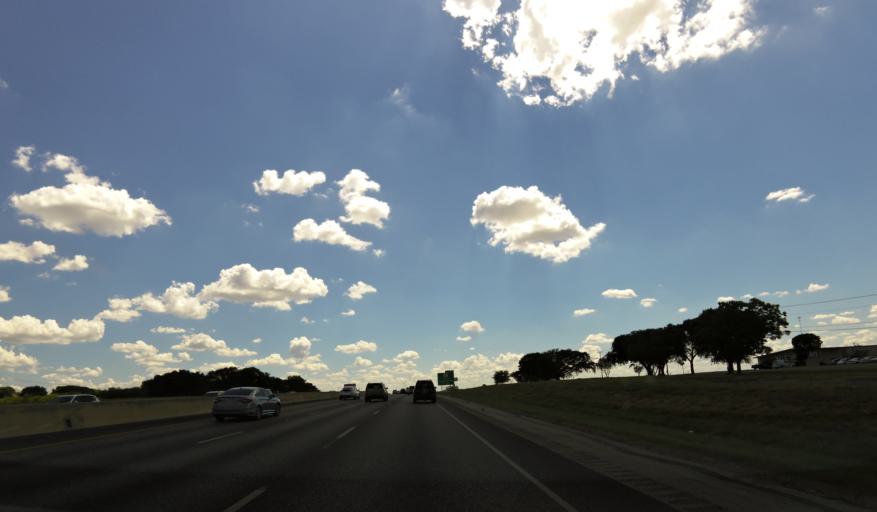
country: US
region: Texas
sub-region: Guadalupe County
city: Northcliff
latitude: 29.6342
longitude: -98.2231
